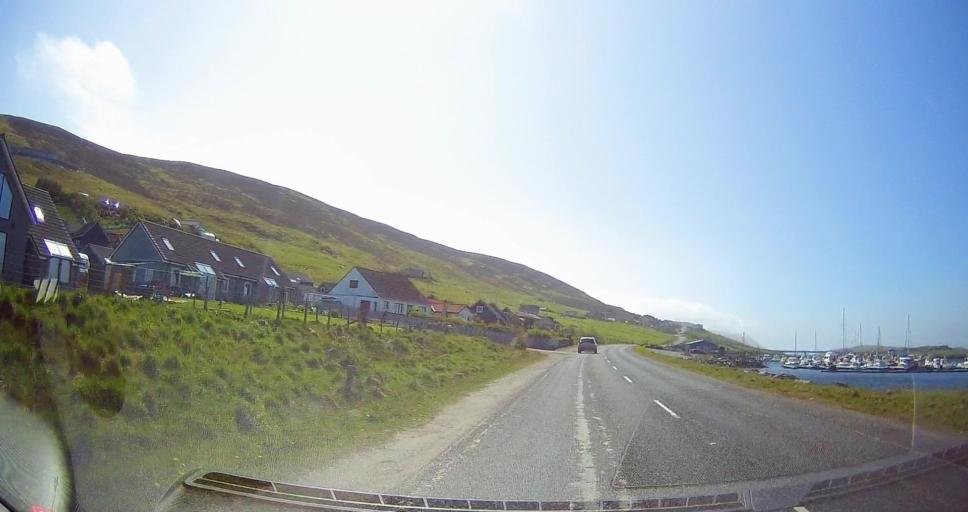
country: GB
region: Scotland
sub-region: Shetland Islands
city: Lerwick
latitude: 60.1387
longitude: -1.2667
